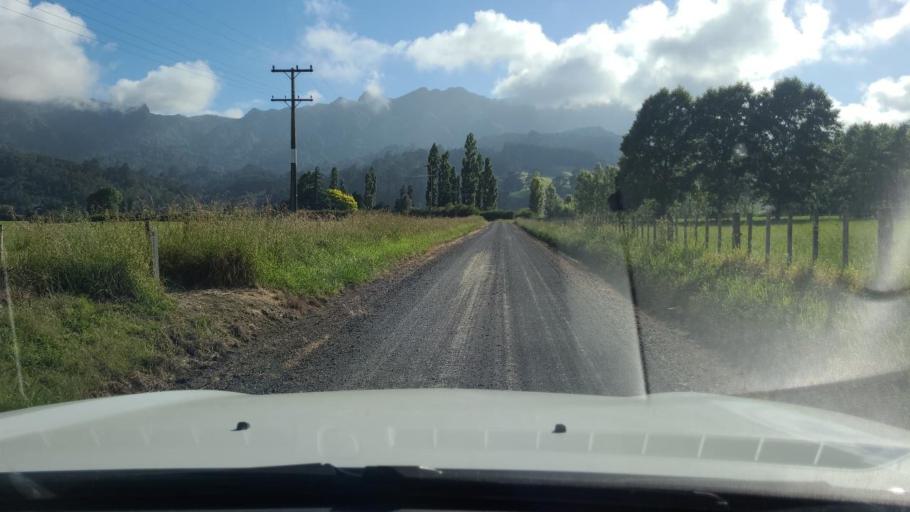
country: NZ
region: Bay of Plenty
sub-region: Western Bay of Plenty District
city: Katikati
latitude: -37.5761
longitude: 175.7598
